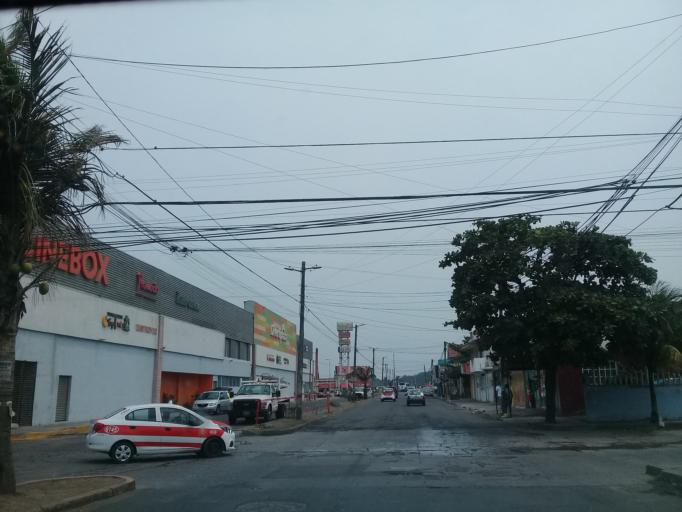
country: MX
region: Veracruz
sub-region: Veracruz
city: Rio Medio [Granja]
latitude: 19.2116
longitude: -96.2001
